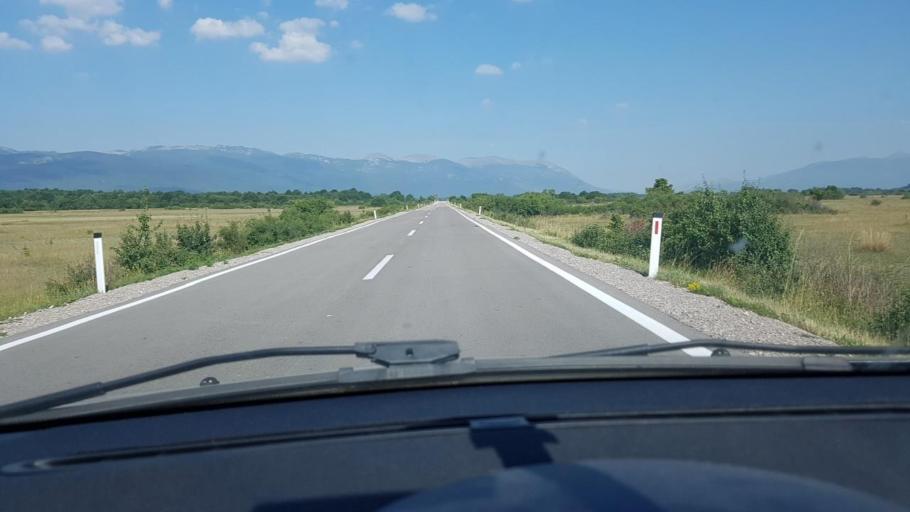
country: BA
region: Federation of Bosnia and Herzegovina
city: Glamoc
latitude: 43.9715
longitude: 16.7224
